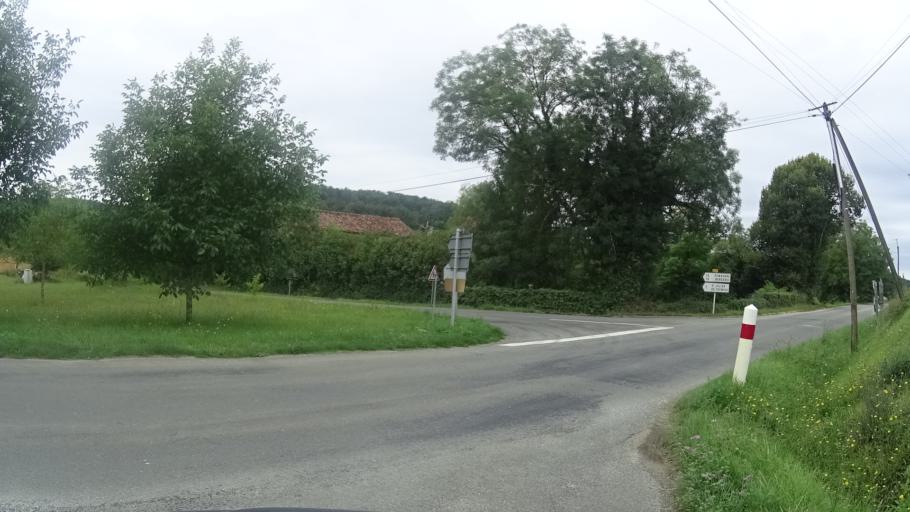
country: FR
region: Aquitaine
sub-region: Departement de la Dordogne
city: Lembras
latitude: 44.9960
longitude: 0.5283
